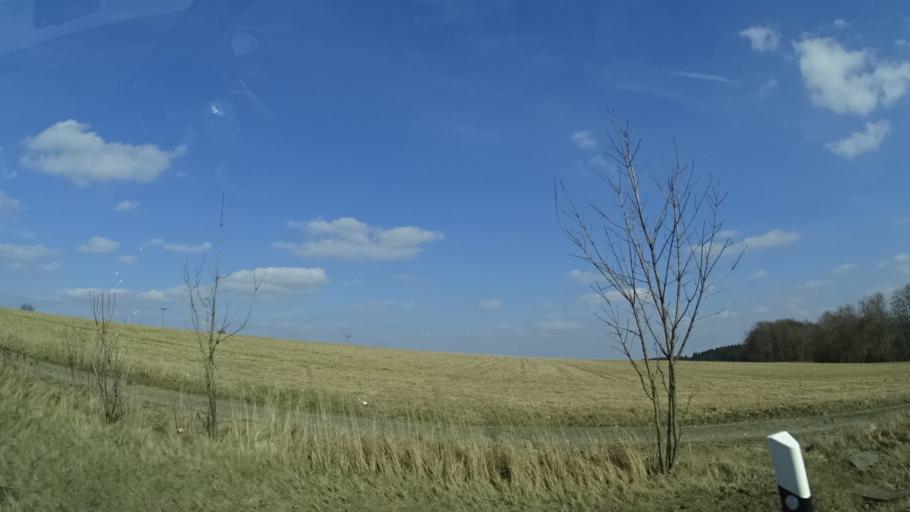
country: DE
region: Thuringia
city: Dreba
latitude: 50.6826
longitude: 11.7799
